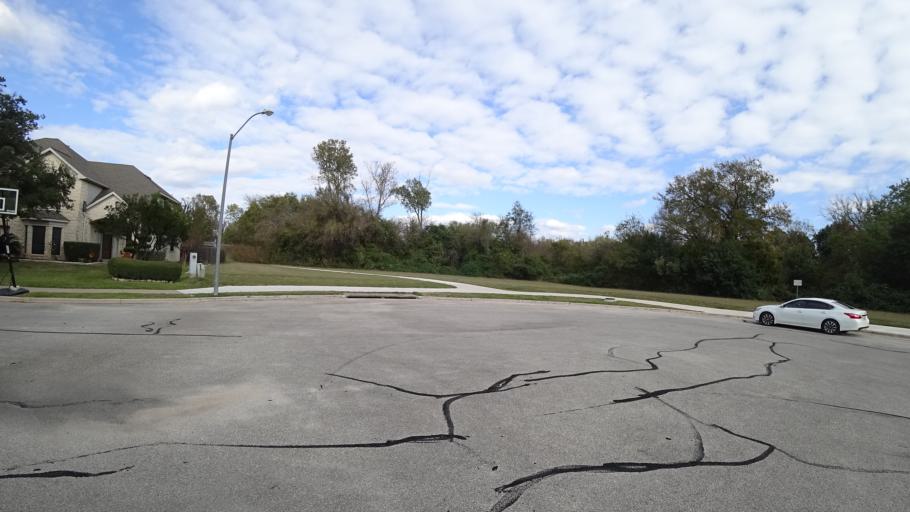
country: US
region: Texas
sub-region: Travis County
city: Pflugerville
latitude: 30.4301
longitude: -97.6245
